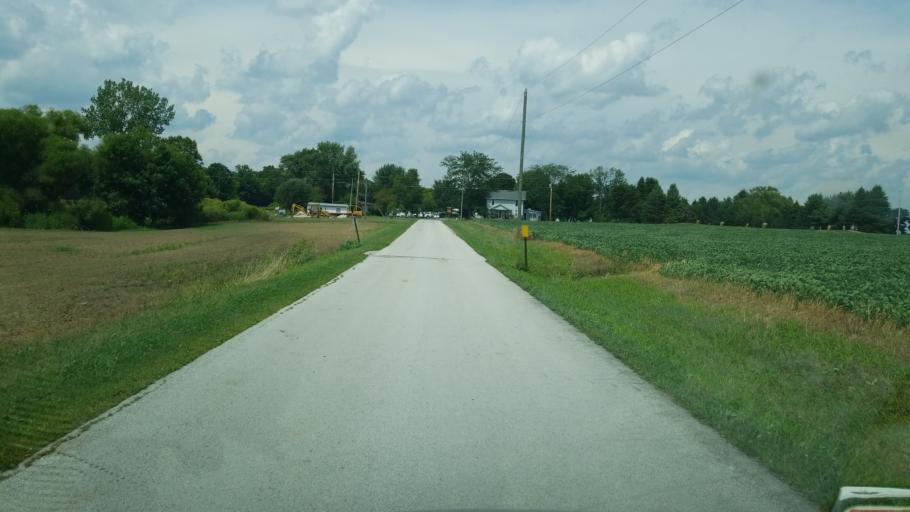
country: US
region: Ohio
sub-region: Hancock County
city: Arlington
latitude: 40.9374
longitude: -83.5438
